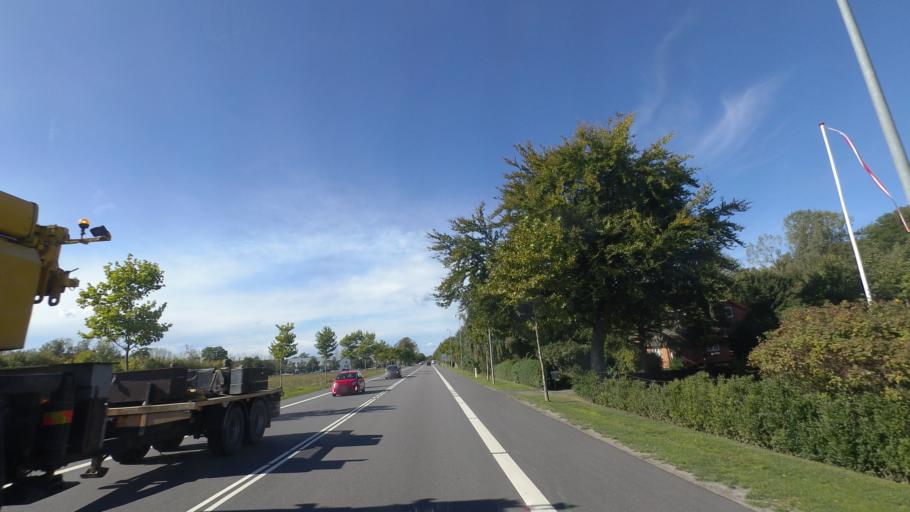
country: DK
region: Capital Region
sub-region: Bornholm Kommune
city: Ronne
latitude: 55.0914
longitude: 14.7336
